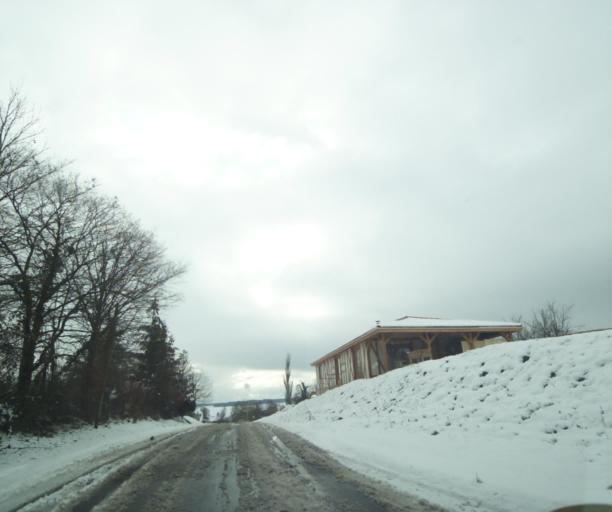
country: FR
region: Champagne-Ardenne
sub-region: Departement de la Haute-Marne
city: Montier-en-Der
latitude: 48.4548
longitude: 4.6941
